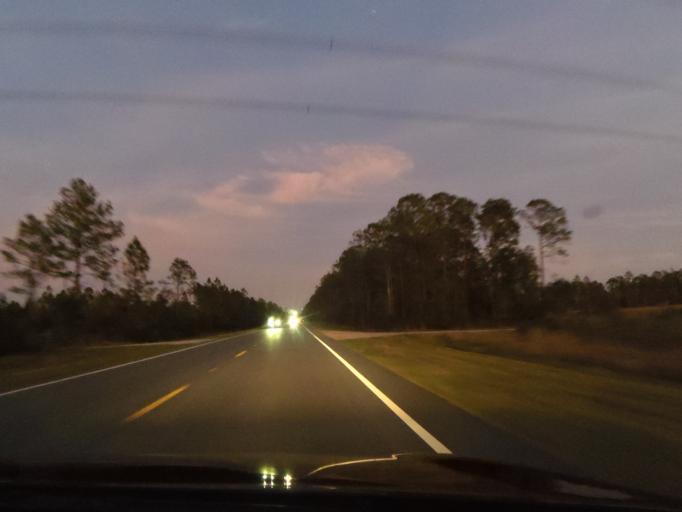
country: US
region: Florida
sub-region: Volusia County
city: De Leon Springs
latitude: 29.2371
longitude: -81.2646
